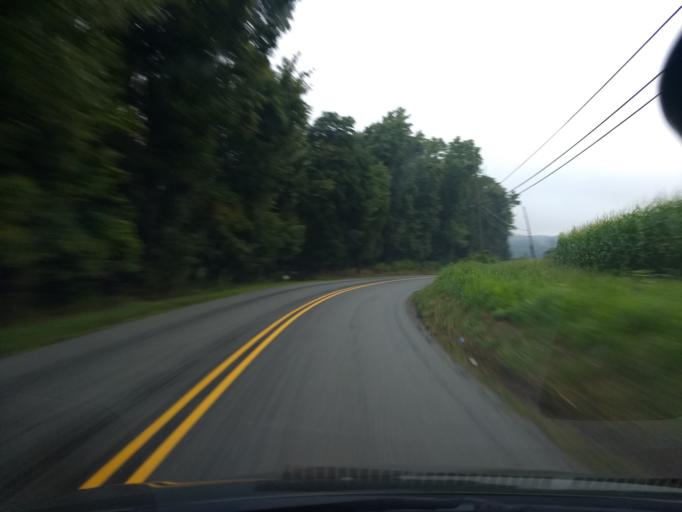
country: US
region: Pennsylvania
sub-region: Westmoreland County
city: Greensburg
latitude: 40.3467
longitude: -79.5052
